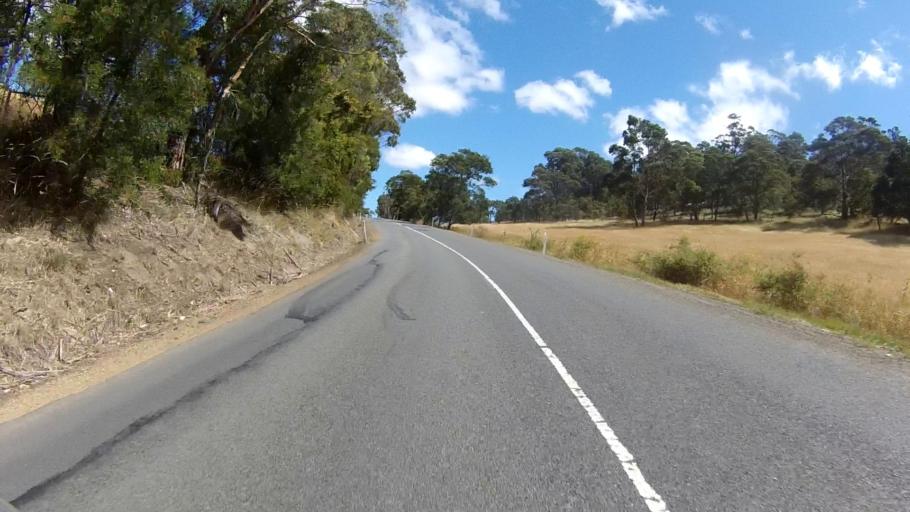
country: AU
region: Tasmania
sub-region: Sorell
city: Sorell
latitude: -42.7361
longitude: 147.4806
